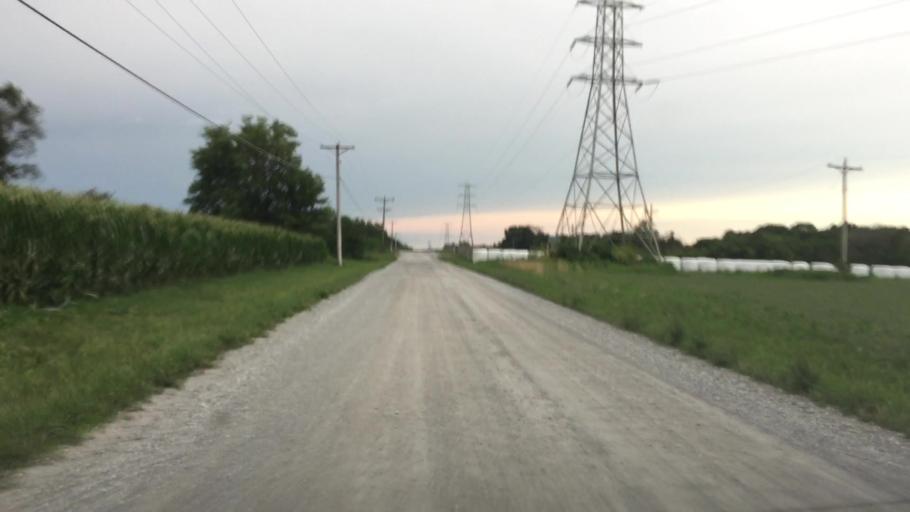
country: US
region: Illinois
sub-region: Hancock County
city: Hamilton
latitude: 40.3725
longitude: -91.3613
